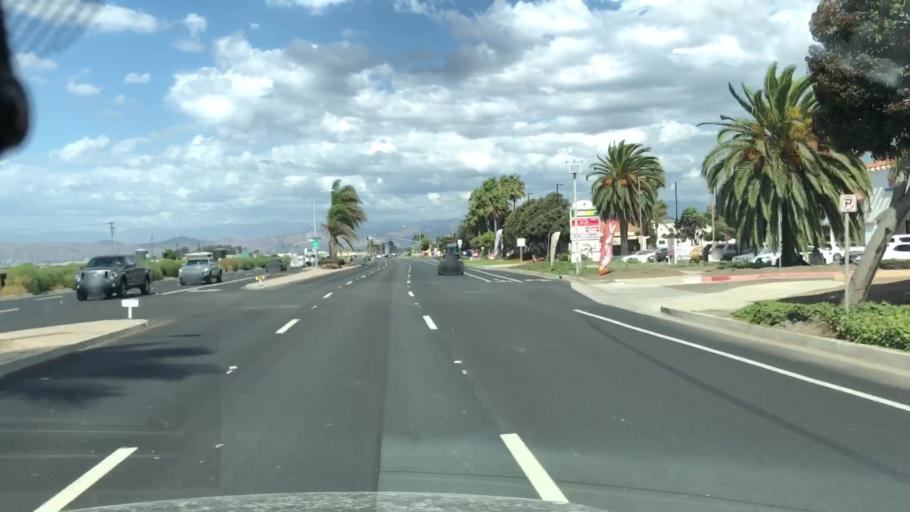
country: US
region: California
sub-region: Ventura County
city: Oxnard Shores
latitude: 34.1954
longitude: -119.2211
